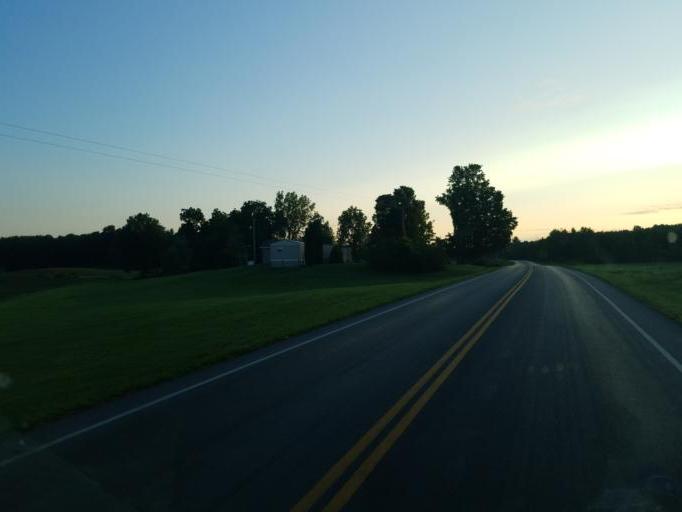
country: US
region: New York
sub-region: Wayne County
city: Clyde
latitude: 43.0601
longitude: -76.8948
